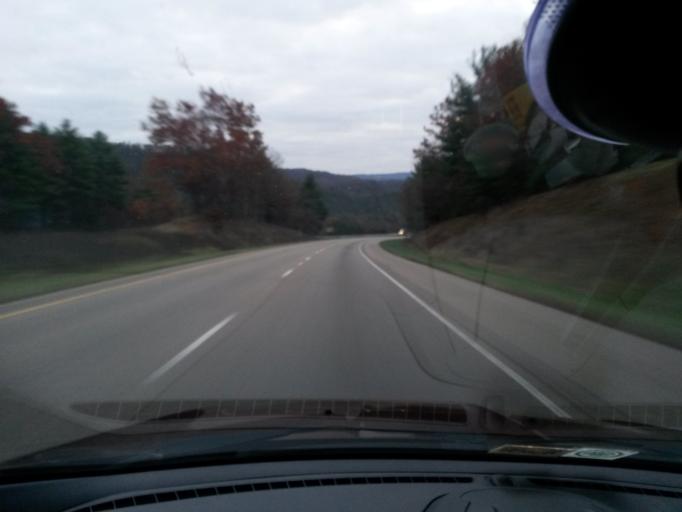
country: US
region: Virginia
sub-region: Alleghany County
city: Clifton Forge
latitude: 37.8218
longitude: -79.7449
